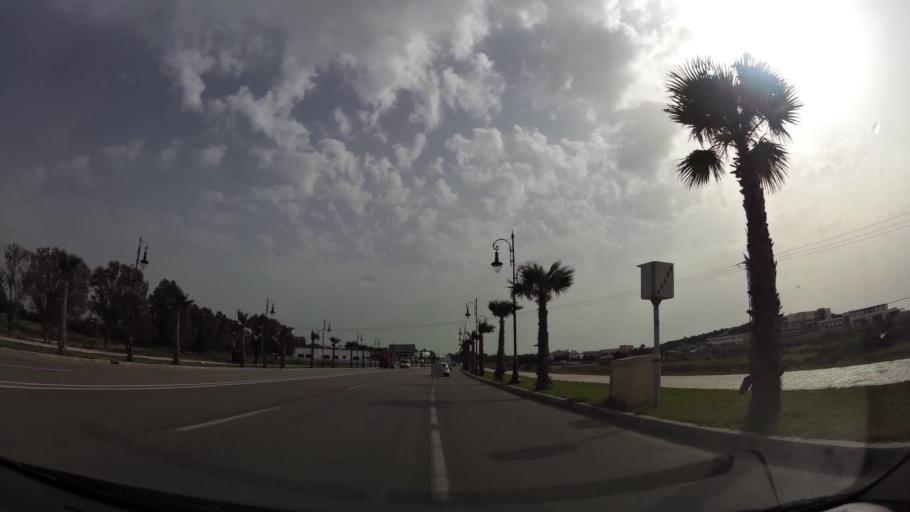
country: MA
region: Tanger-Tetouan
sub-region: Tanger-Assilah
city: Boukhalef
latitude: 35.6877
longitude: -5.9174
